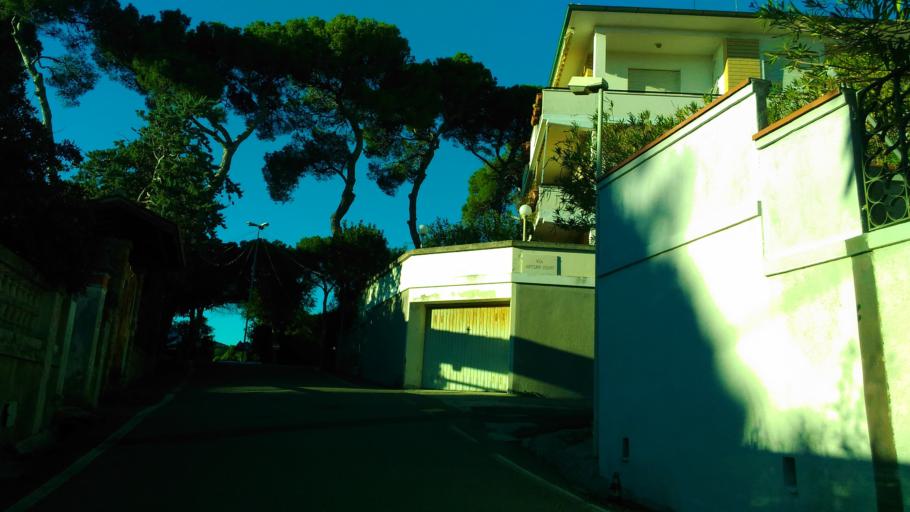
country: IT
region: Tuscany
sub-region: Provincia di Livorno
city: Quercianella
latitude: 43.4572
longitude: 10.3687
